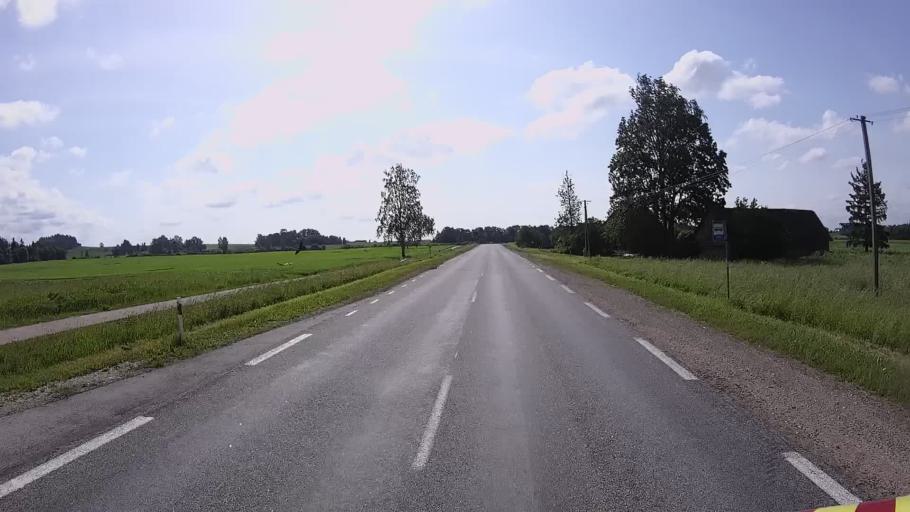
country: EE
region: Vorumaa
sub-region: Antsla vald
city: Vana-Antsla
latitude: 57.9447
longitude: 26.2997
